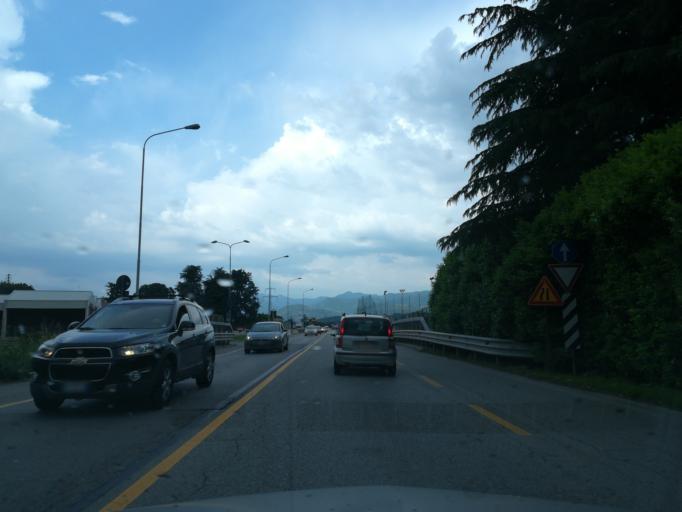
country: IT
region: Lombardy
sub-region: Provincia di Bergamo
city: Mozzo
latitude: 45.7016
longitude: 9.6047
